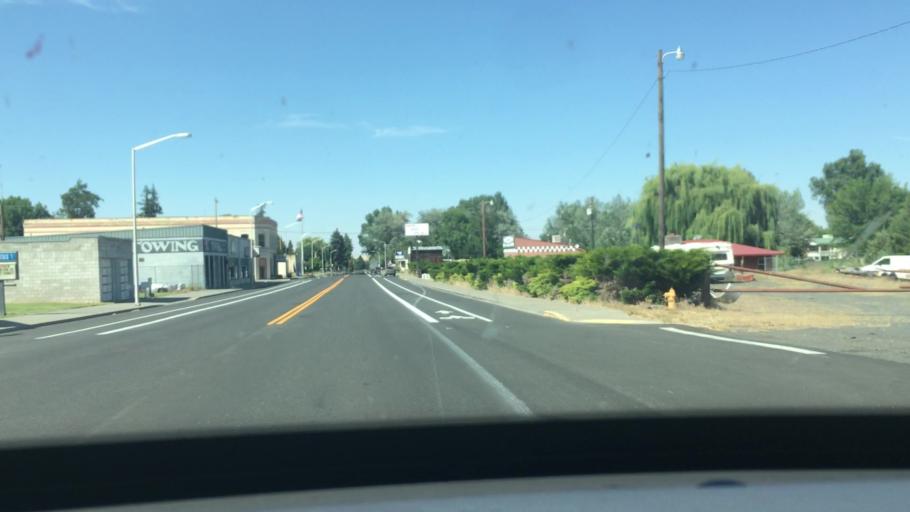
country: US
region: Oregon
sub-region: Sherman County
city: Moro
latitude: 45.3592
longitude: -120.7851
